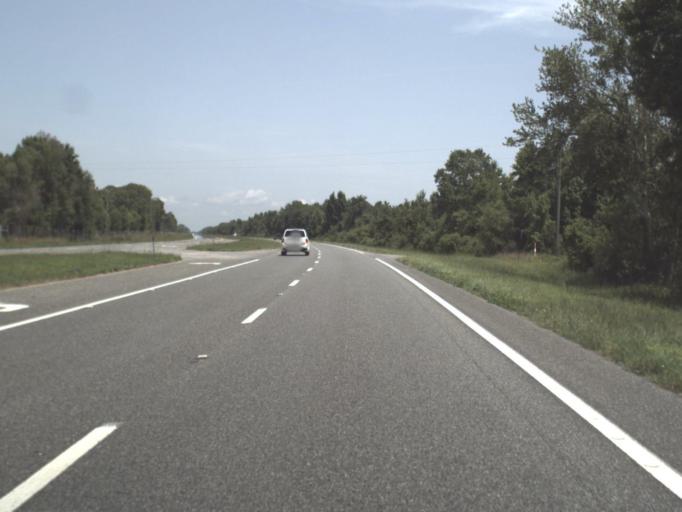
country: US
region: Florida
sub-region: Taylor County
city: Steinhatchee
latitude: 29.8138
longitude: -83.3461
